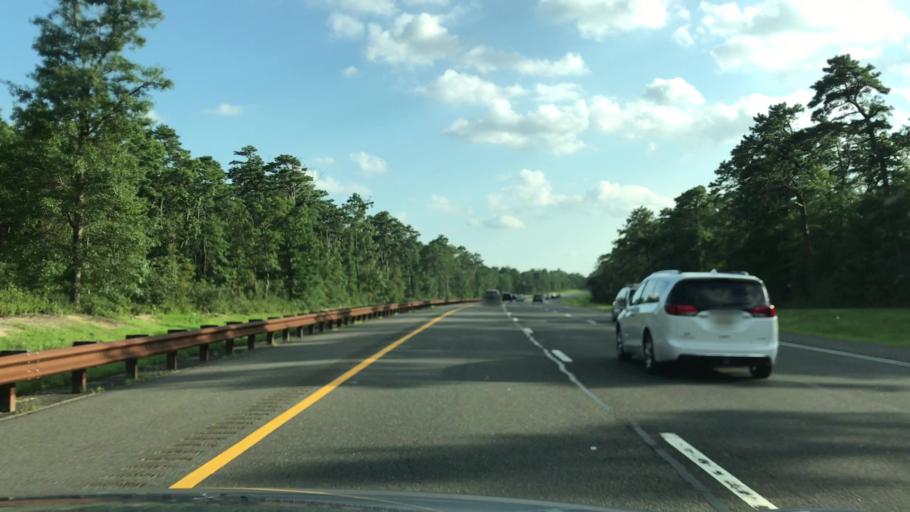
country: US
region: New Jersey
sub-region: Ocean County
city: Manahawkin
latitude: 39.6840
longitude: -74.3036
